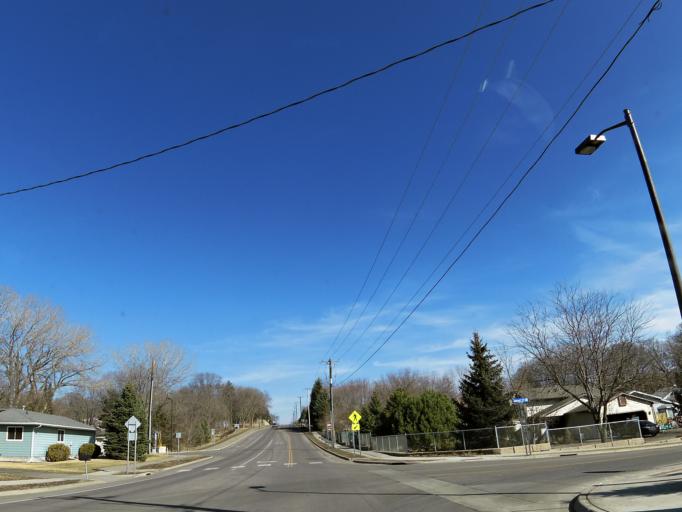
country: US
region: Minnesota
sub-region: Scott County
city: Prior Lake
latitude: 44.7030
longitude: -93.4560
